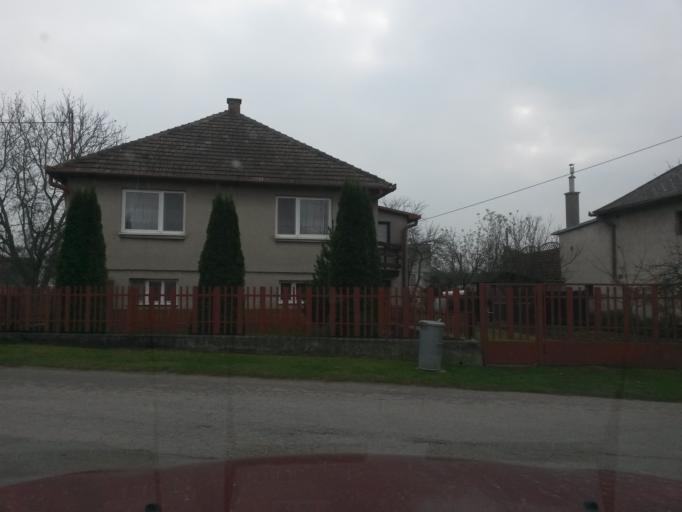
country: SK
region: Presovsky
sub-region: Okres Presov
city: Presov
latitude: 48.8728
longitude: 21.2672
